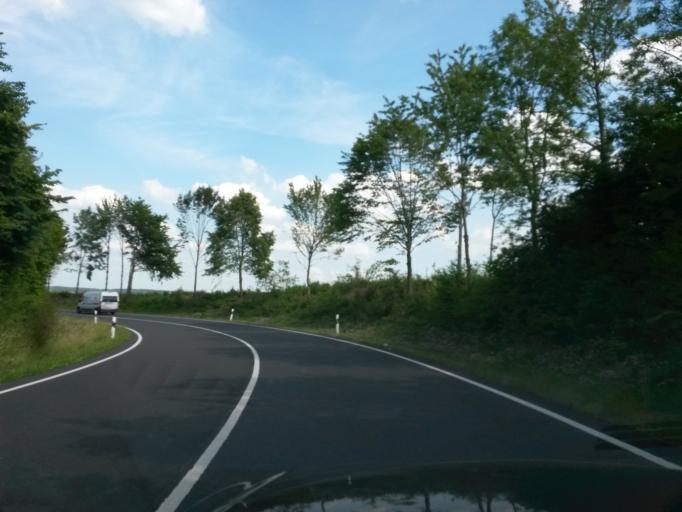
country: DE
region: Bavaria
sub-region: Regierungsbezirk Unterfranken
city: Kurnach
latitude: 49.8550
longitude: 10.0195
